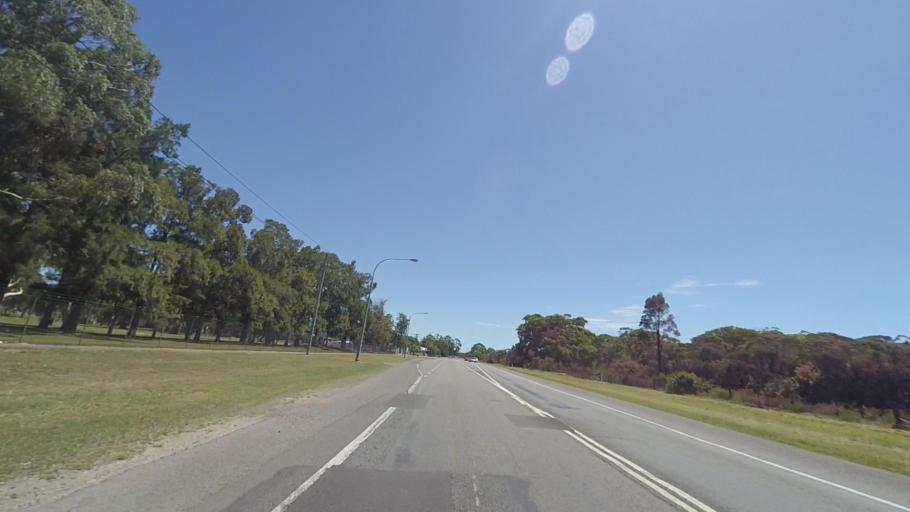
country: AU
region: New South Wales
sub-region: Port Stephens Shire
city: Medowie
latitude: -32.7952
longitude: 151.8528
